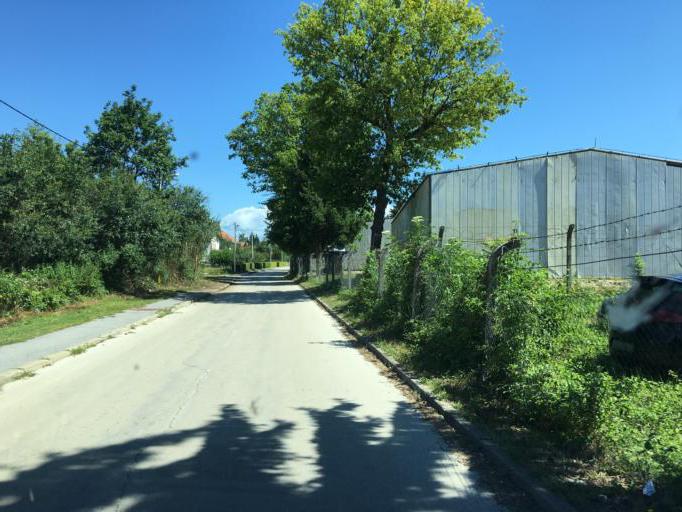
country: HR
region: Licko-Senjska
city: Gospic
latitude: 44.5476
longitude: 15.3584
